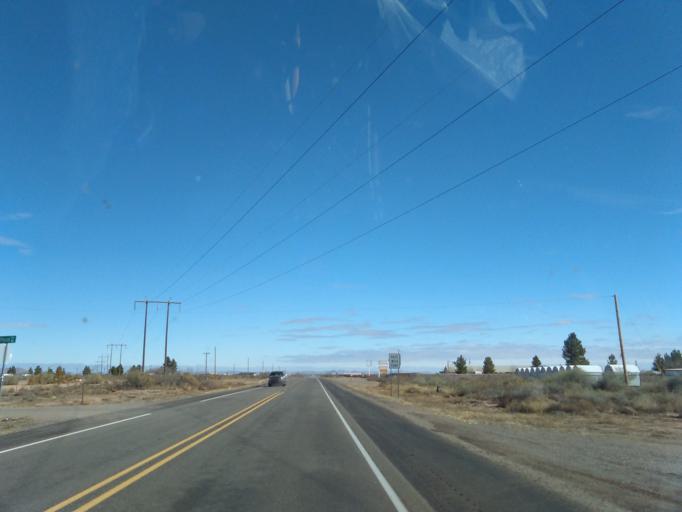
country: US
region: New Mexico
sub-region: Luna County
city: Deming
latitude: 32.2938
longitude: -107.7367
